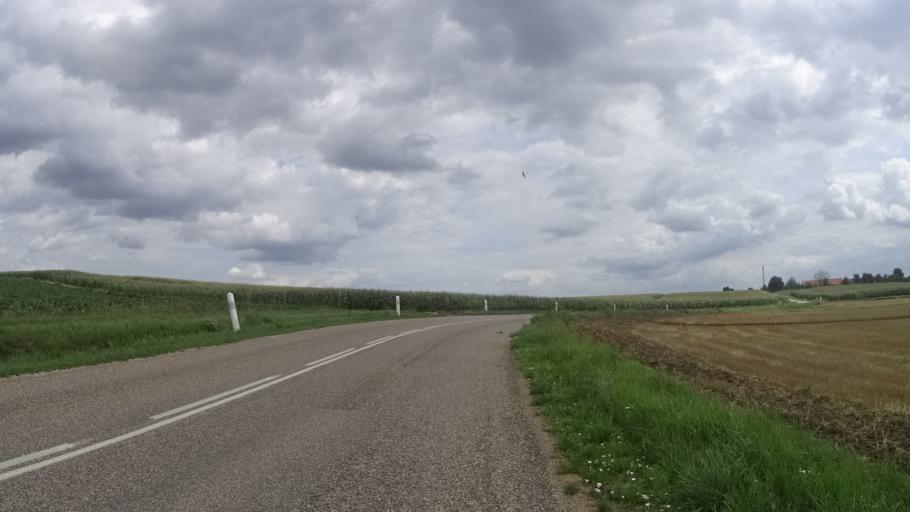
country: FR
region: Alsace
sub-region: Departement du Bas-Rhin
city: Hoerdt
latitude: 48.7217
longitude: 7.7753
